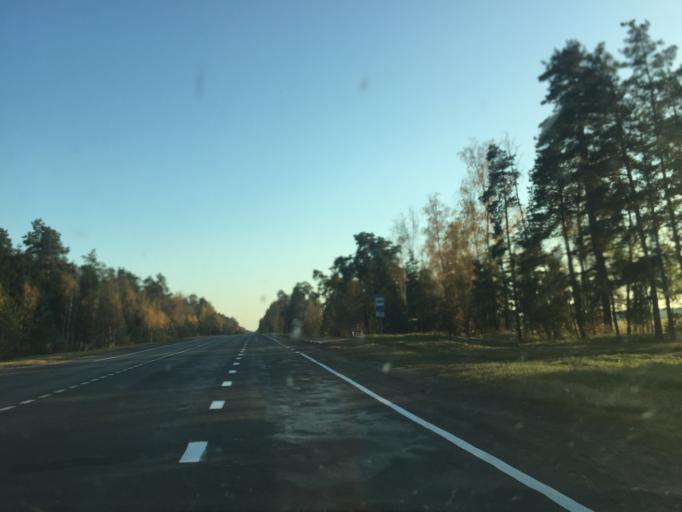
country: BY
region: Mogilev
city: Poselok Voskhod
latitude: 53.7305
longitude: 30.3667
